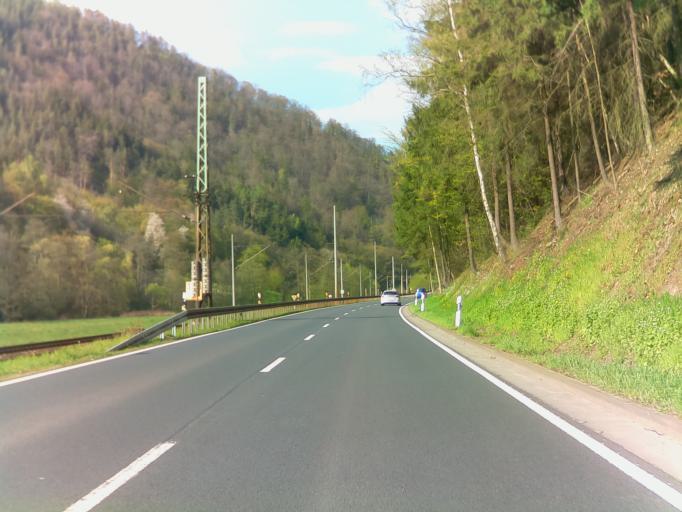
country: DE
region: Thuringia
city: Leutenberg
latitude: 50.5901
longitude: 11.4230
